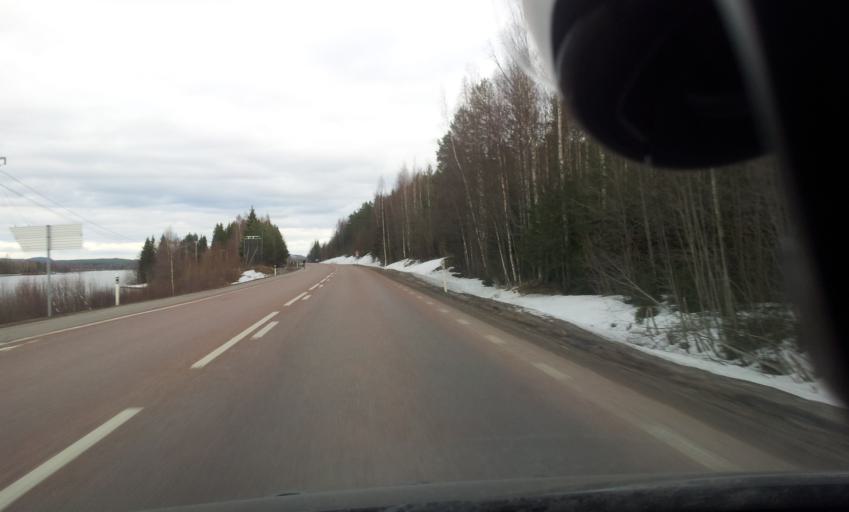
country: SE
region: Gaevleborg
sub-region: Ljusdals Kommun
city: Ljusdal
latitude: 61.8180
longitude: 16.0693
